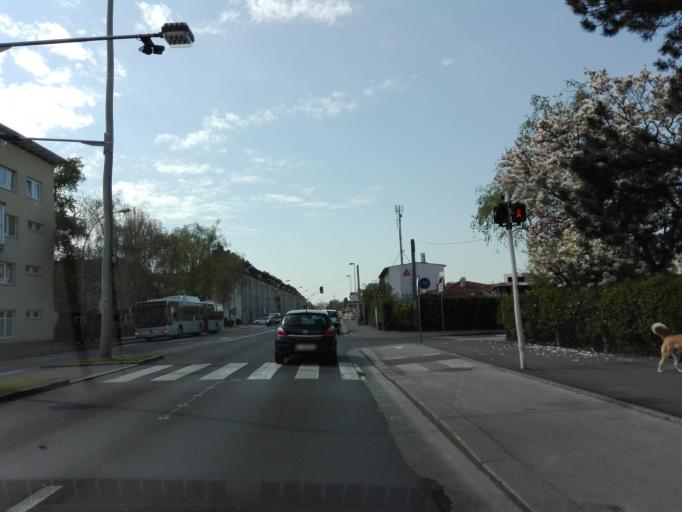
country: AT
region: Upper Austria
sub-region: Politischer Bezirk Linz-Land
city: Ansfelden
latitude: 48.2526
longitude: 14.2934
